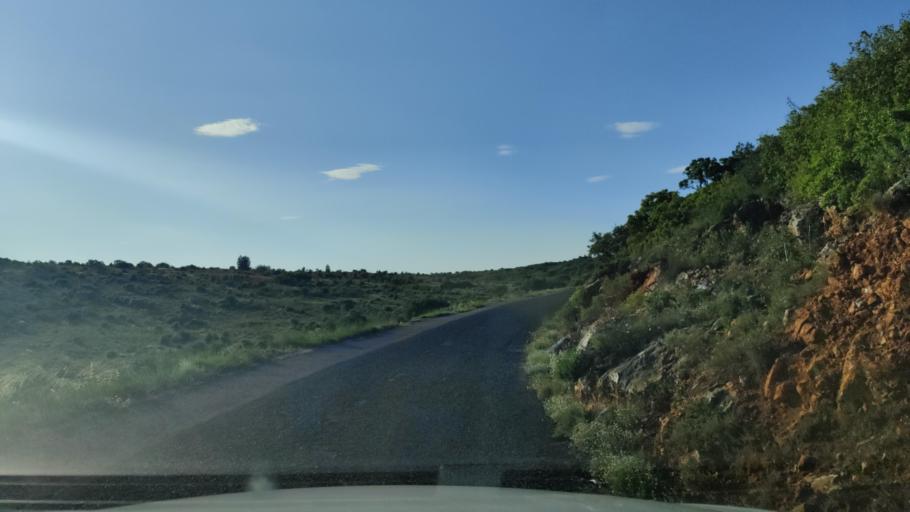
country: FR
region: Languedoc-Roussillon
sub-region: Departement des Pyrenees-Orientales
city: Estagel
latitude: 42.7860
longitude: 2.7447
